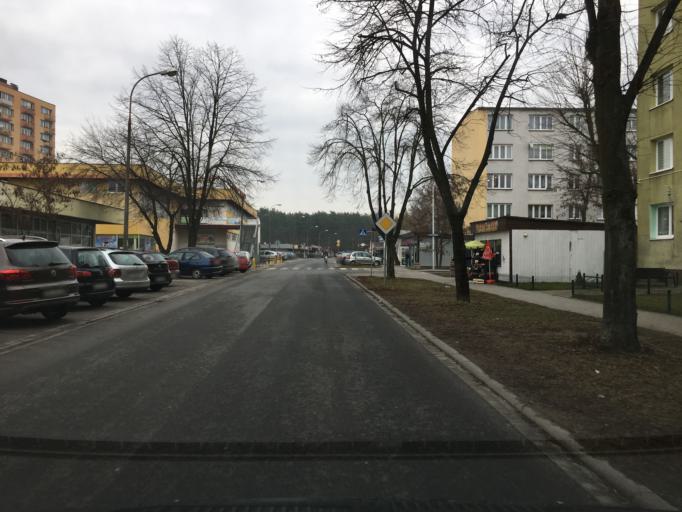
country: PL
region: Opole Voivodeship
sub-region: Powiat kedzierzynsko-kozielski
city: Kedzierzyn-Kozle
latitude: 50.3453
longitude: 18.2217
